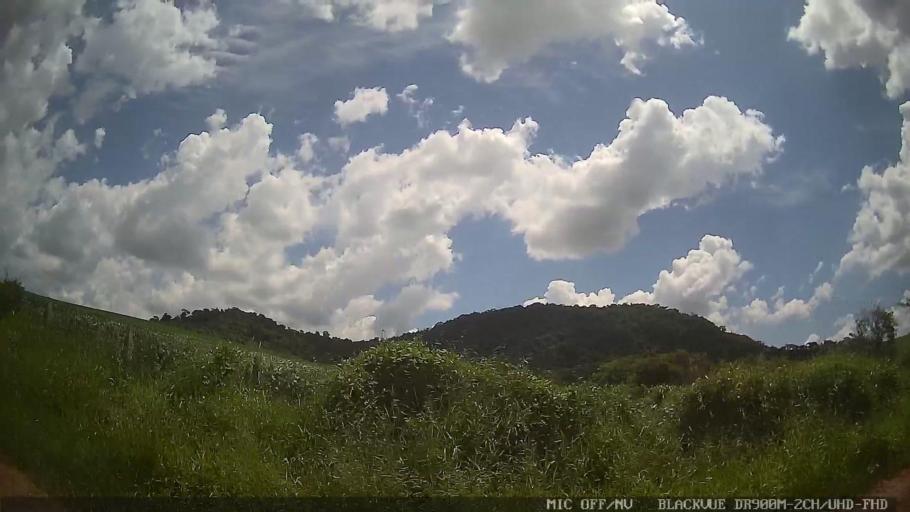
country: BR
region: Sao Paulo
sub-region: Atibaia
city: Atibaia
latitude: -23.0993
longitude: -46.6339
